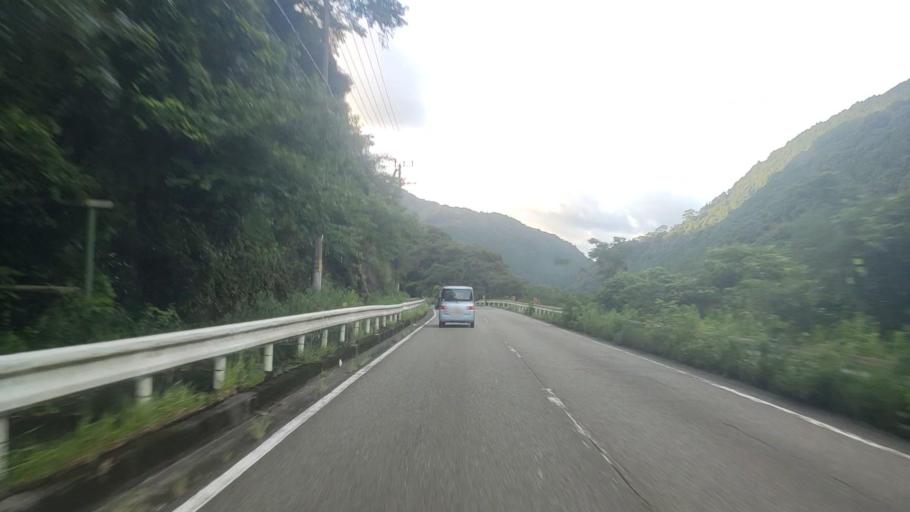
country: JP
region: Wakayama
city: Tanabe
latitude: 33.7650
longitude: 135.5002
